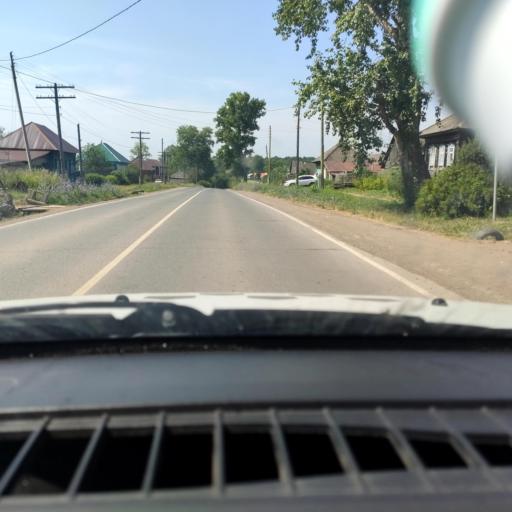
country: RU
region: Perm
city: Okhansk
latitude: 57.7103
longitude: 55.3246
